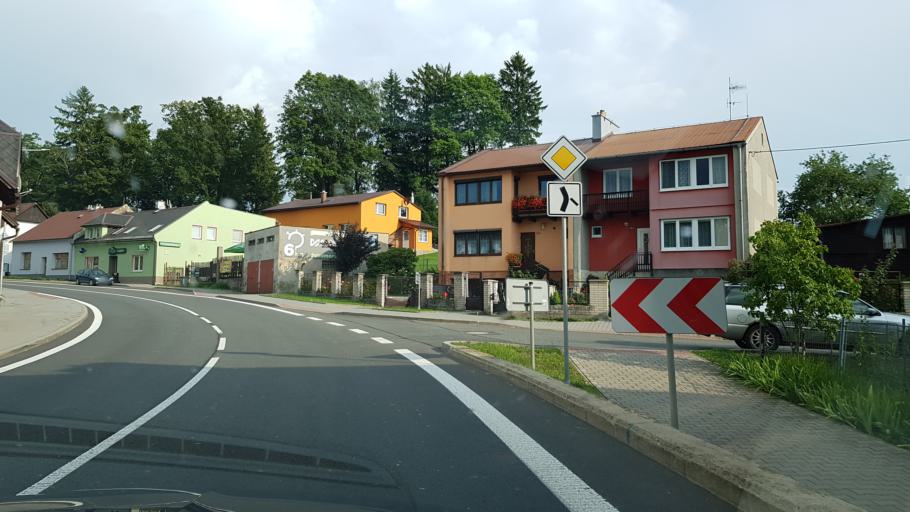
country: CZ
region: Pardubicky
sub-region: Okres Usti nad Orlici
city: Kraliky
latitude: 50.0828
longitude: 16.7492
